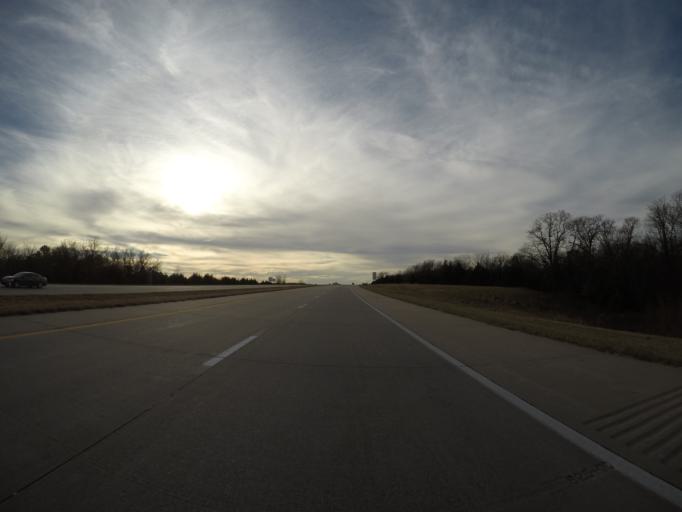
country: US
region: Kansas
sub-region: Franklin County
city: Ottawa
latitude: 38.5309
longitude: -95.3879
